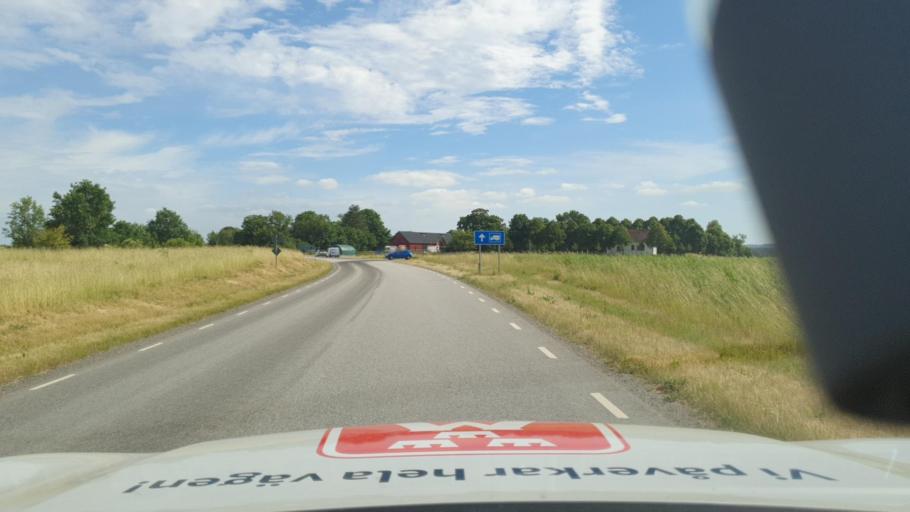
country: SE
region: Skane
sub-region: Sjobo Kommun
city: Sjoebo
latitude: 55.6196
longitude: 13.6535
